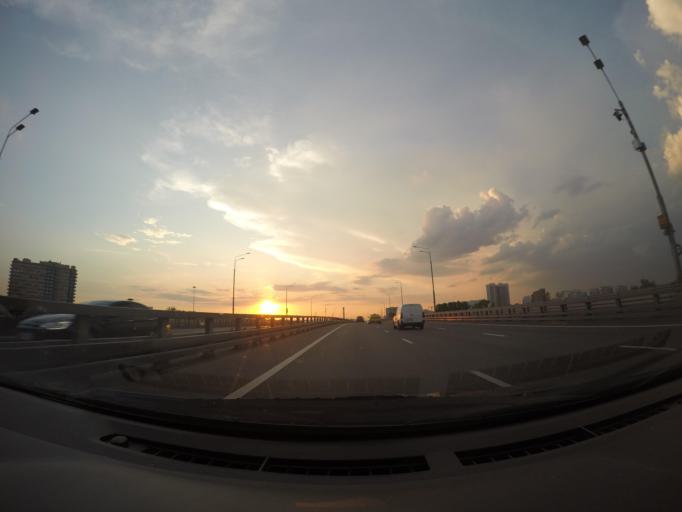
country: RU
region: Moscow
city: Ryazanskiy
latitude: 55.7334
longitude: 37.7718
